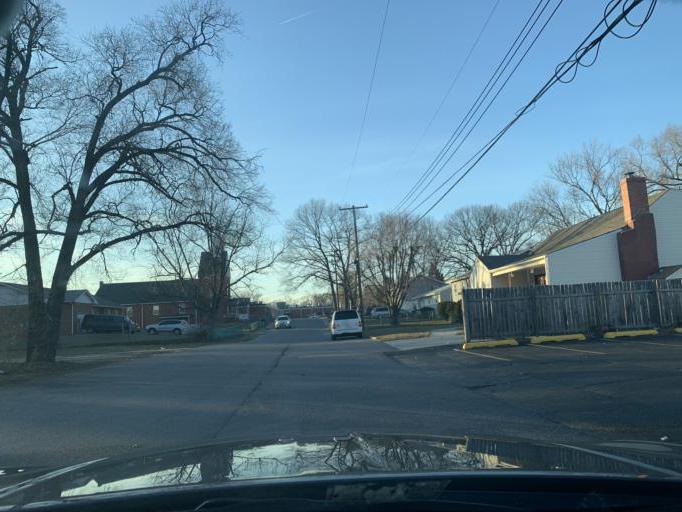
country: US
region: Maryland
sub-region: Anne Arundel County
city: Glen Burnie
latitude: 39.1548
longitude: -76.6311
